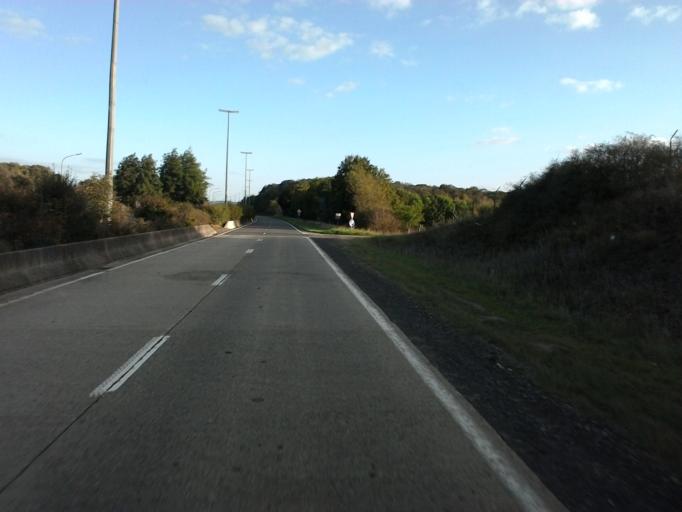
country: BE
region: Wallonia
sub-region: Province de Namur
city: Somme-Leuze
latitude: 50.3115
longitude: 5.3403
